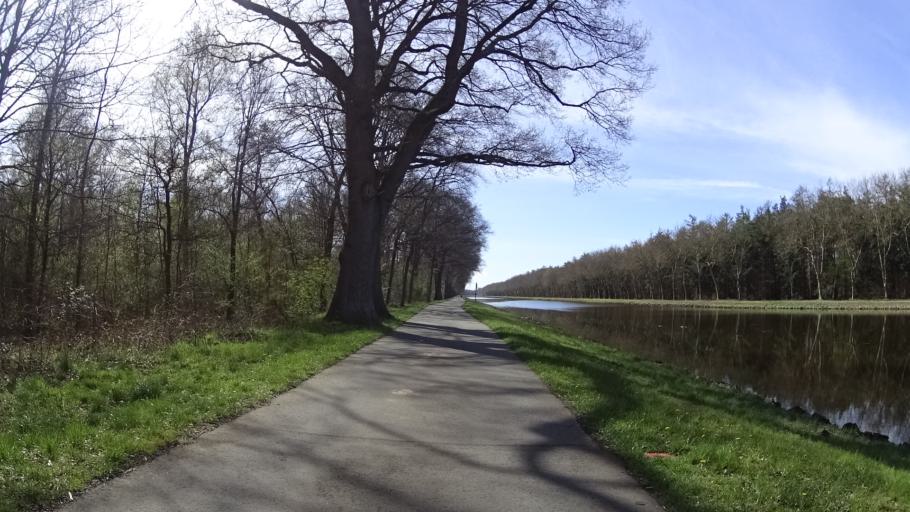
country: DE
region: Lower Saxony
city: Geeste
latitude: 52.5928
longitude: 7.3105
